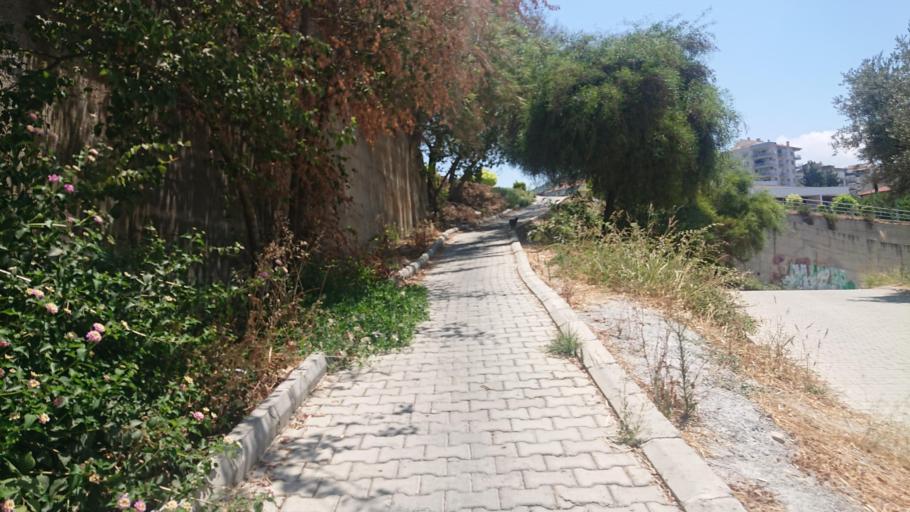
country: TR
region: Aydin
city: Kusadasi
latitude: 37.8692
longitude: 27.2676
